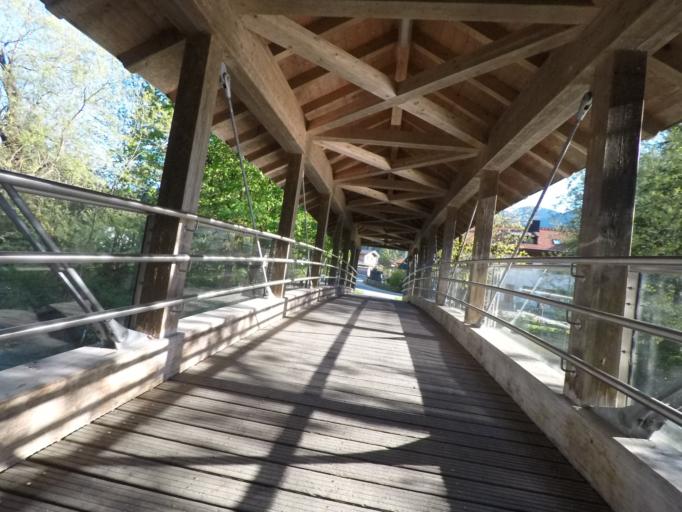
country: DE
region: Bavaria
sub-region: Upper Bavaria
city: Fischbachau
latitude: 47.7068
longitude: 11.9362
